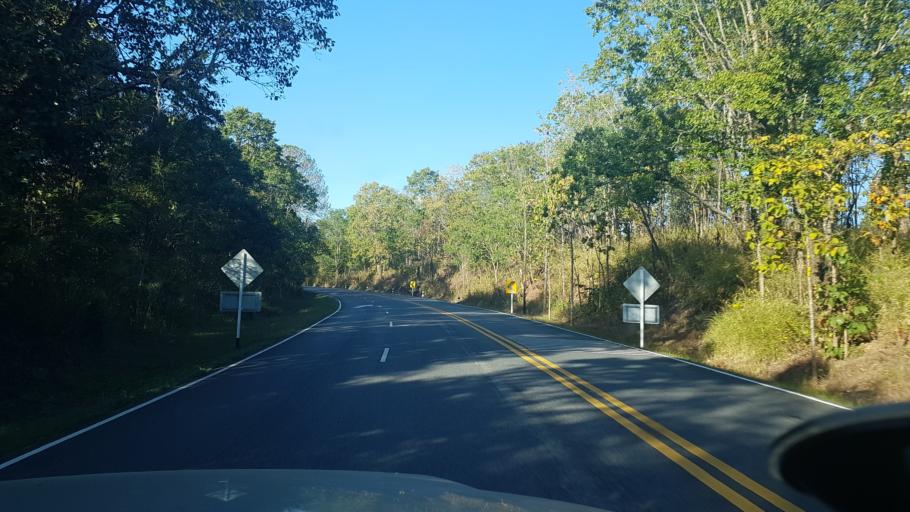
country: TH
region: Phetchabun
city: Nam Nao
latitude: 16.7023
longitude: 101.6461
